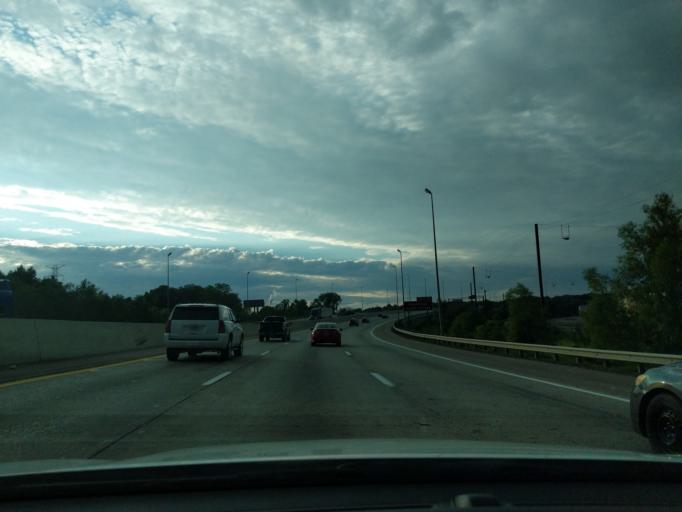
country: US
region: Tennessee
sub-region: Shelby County
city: New South Memphis
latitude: 35.0807
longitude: -90.0720
